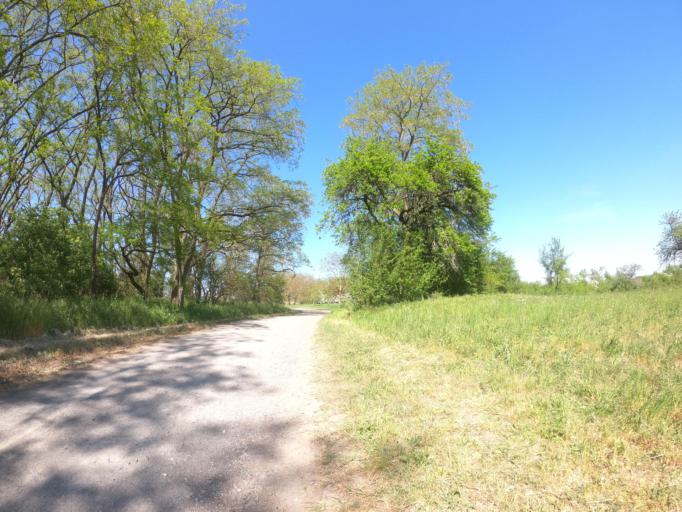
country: DE
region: Hesse
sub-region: Regierungsbezirk Darmstadt
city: Florsheim
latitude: 50.0171
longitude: 8.4019
